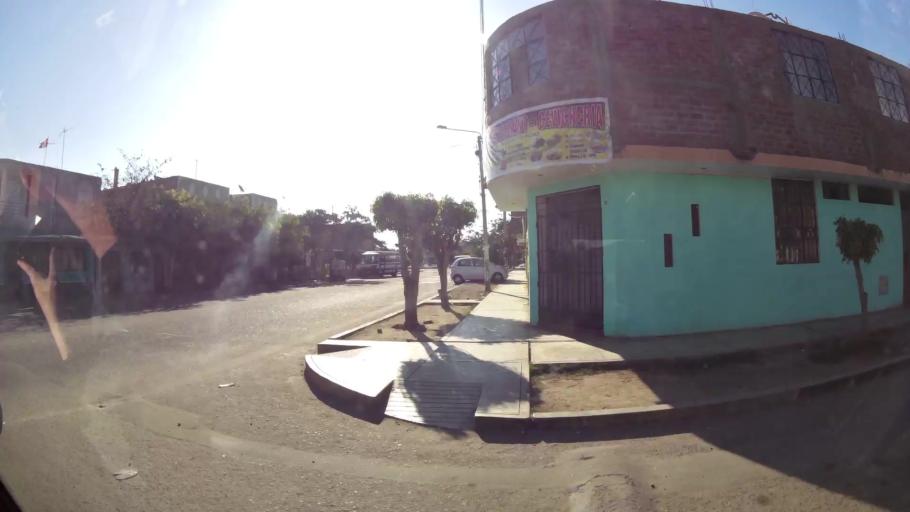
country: PE
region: Ica
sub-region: Provincia de Ica
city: La Tinguina
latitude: -14.0474
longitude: -75.6976
